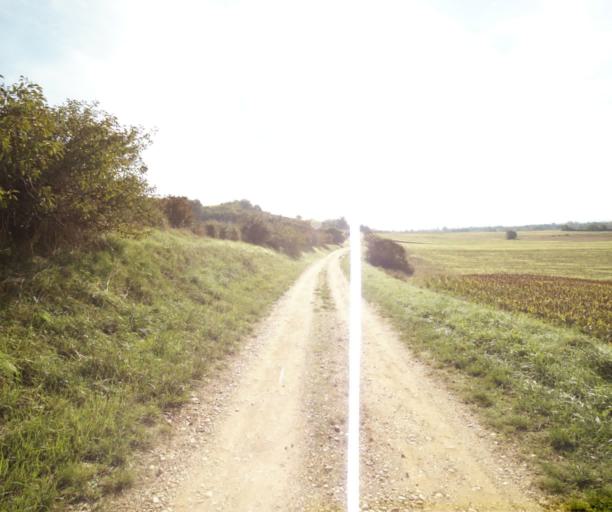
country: FR
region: Midi-Pyrenees
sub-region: Departement du Tarn-et-Garonne
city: Nohic
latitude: 43.9213
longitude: 1.4400
